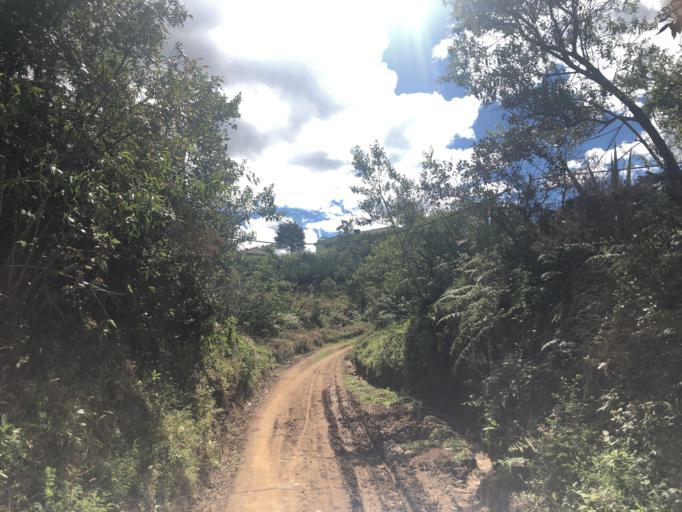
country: CO
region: Cauca
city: Silvia
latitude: 2.6782
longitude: -76.4416
